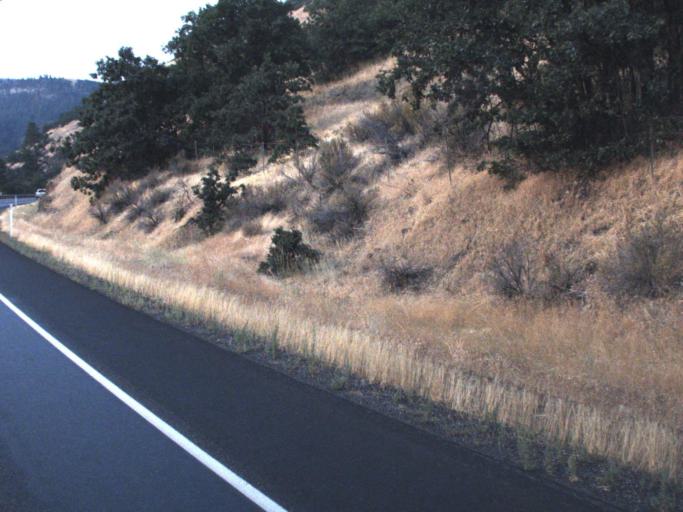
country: US
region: Washington
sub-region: Klickitat County
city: Goldendale
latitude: 46.0514
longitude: -120.5679
